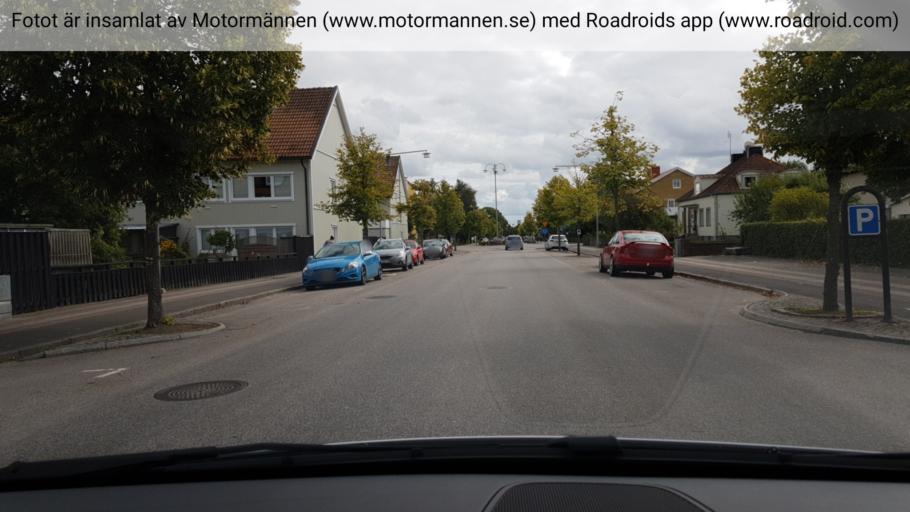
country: SE
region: Vaestra Goetaland
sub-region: Vara Kommun
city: Vara
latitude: 58.2601
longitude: 12.9555
